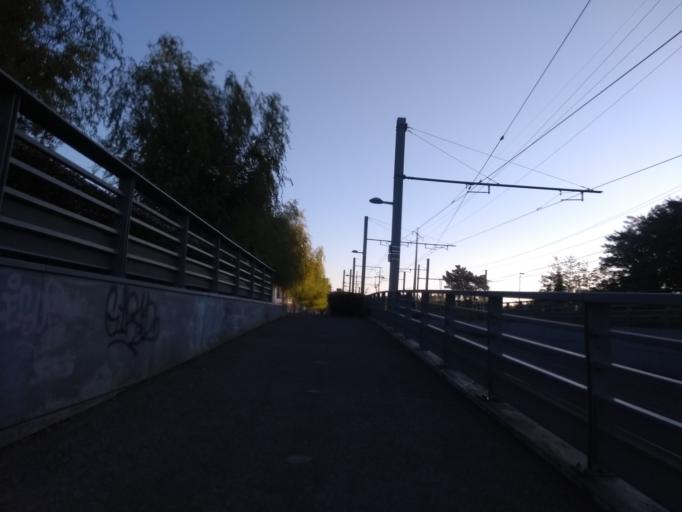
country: FR
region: Aquitaine
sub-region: Departement de la Gironde
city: Pessac
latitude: 44.8037
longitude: -0.6344
